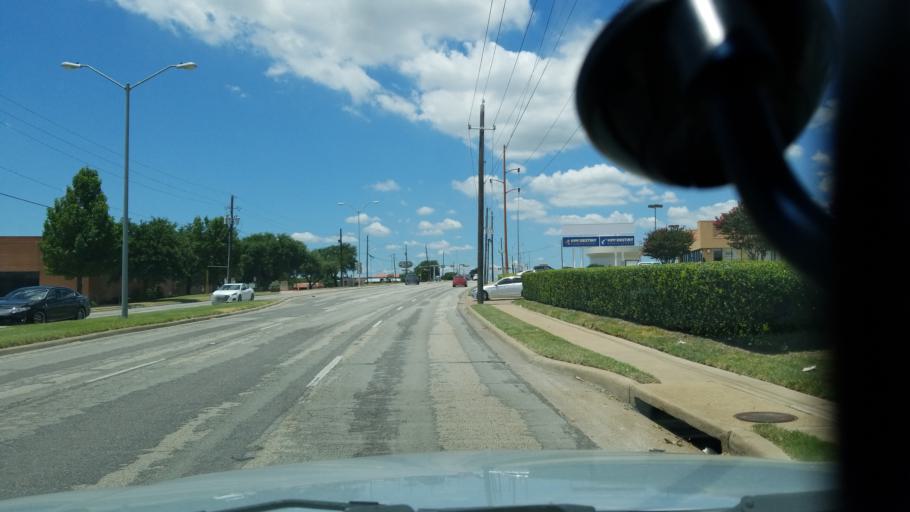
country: US
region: Texas
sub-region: Dallas County
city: Duncanville
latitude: 32.6623
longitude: -96.8790
